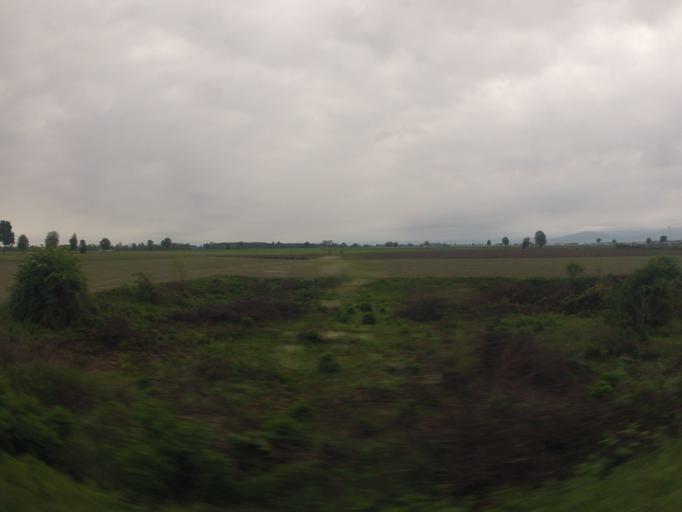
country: IT
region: Piedmont
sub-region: Provincia di Cuneo
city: Faule
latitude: 44.8014
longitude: 7.5851
